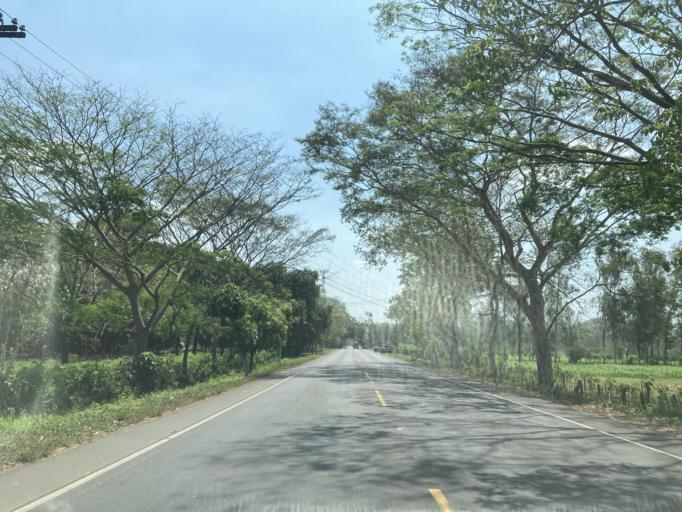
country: GT
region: Escuintla
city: Guanagazapa
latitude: 14.2098
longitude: -90.7202
